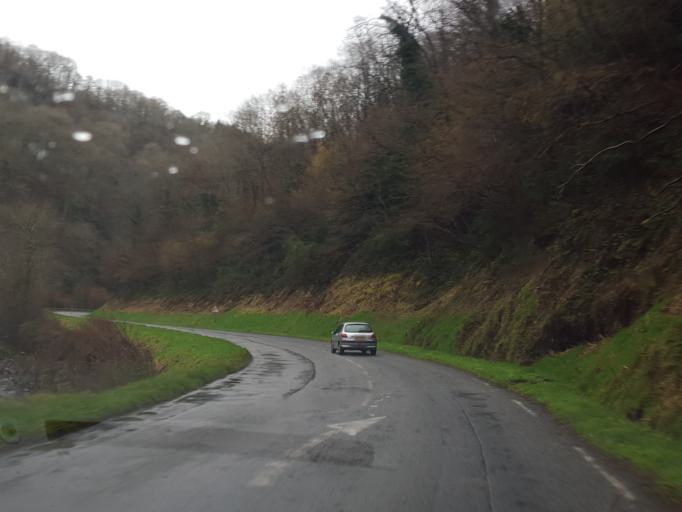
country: FR
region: Midi-Pyrenees
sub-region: Departement de l'Ariege
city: Saint-Girons
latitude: 42.9188
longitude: 1.1893
